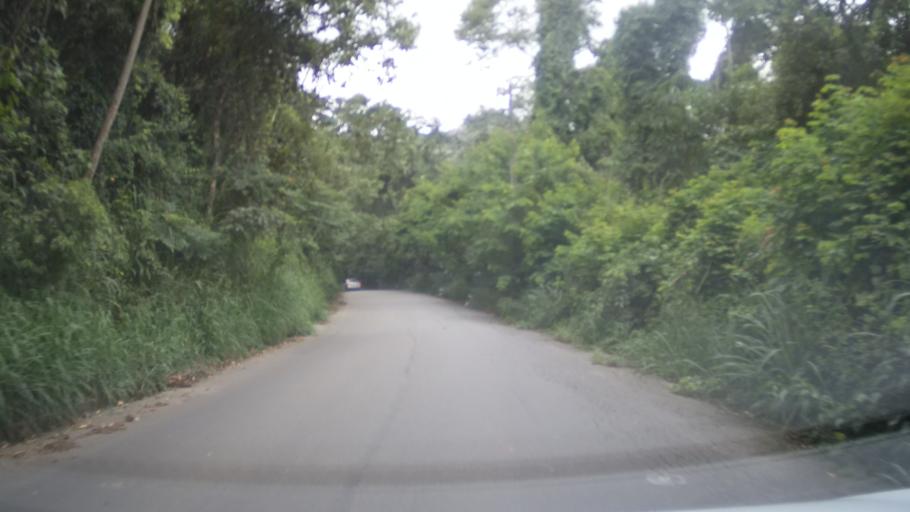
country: BR
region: Sao Paulo
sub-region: Aruja
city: Aruja
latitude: -23.3542
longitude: -46.2860
